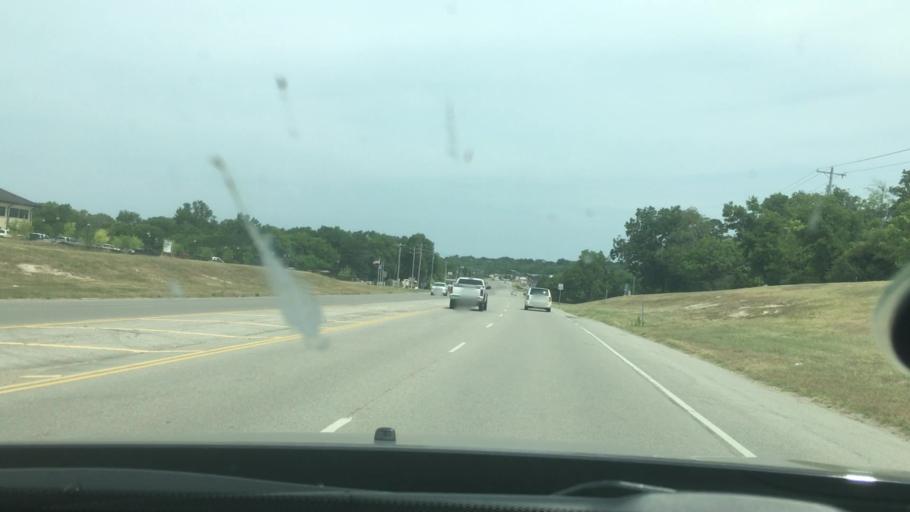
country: US
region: Oklahoma
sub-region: Pontotoc County
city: Ada
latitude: 34.7552
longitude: -96.6587
